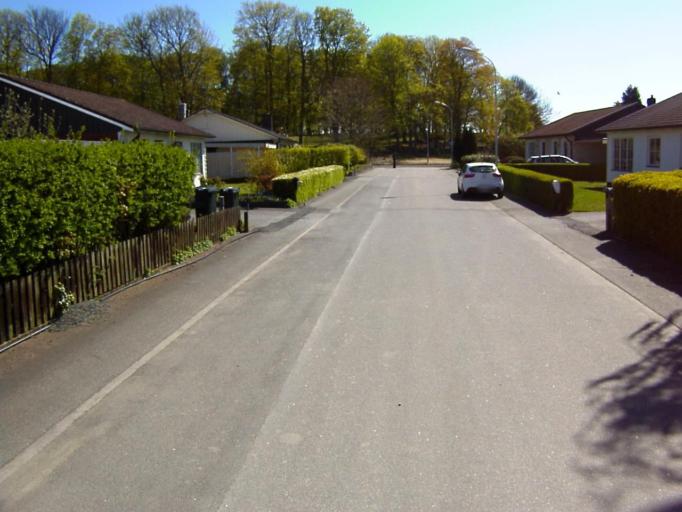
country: SE
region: Skane
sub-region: Kristianstads Kommun
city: Kristianstad
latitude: 56.0276
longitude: 14.1954
